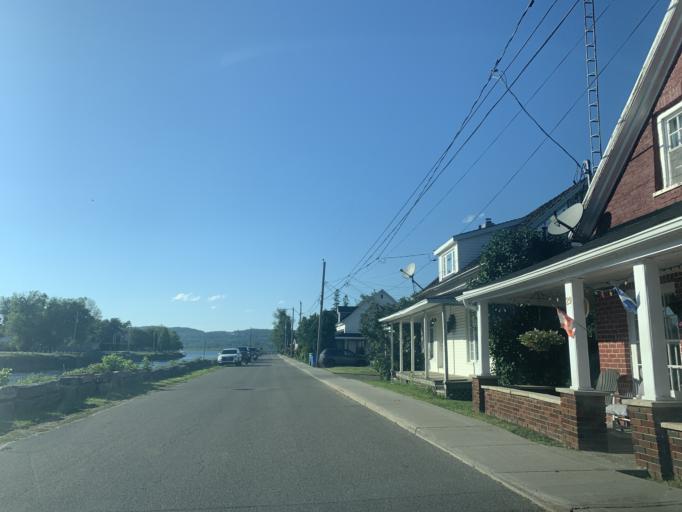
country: CA
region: Ontario
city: Hawkesbury
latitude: 45.6274
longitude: -74.6063
